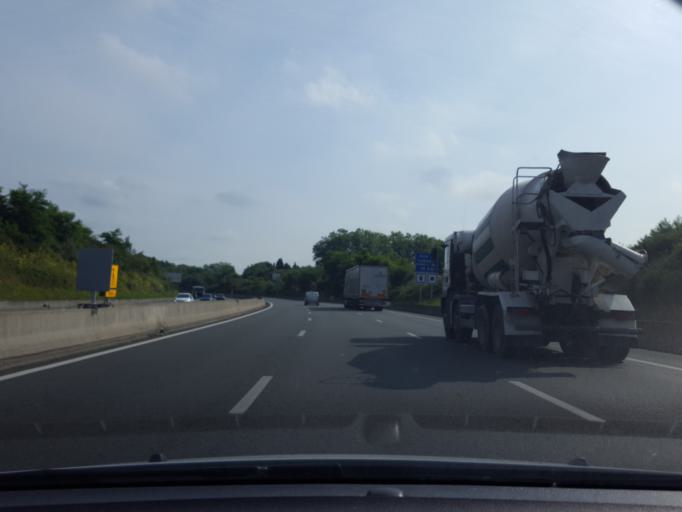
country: FR
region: Aquitaine
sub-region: Departement des Pyrenees-Atlantiques
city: Boucau
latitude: 43.4982
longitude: -1.4434
